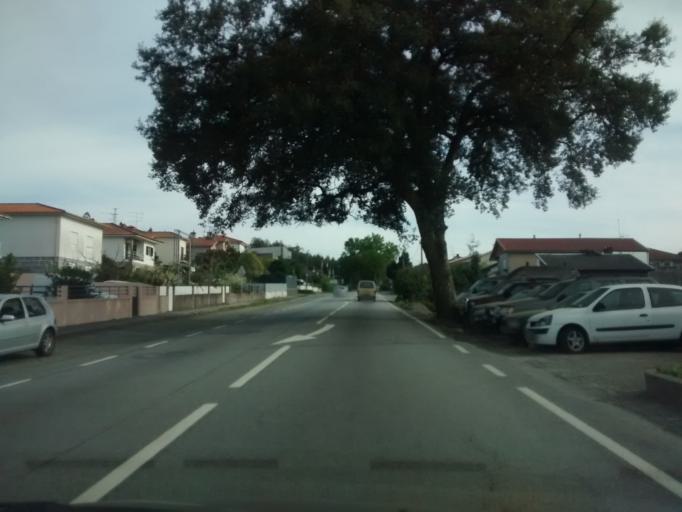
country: PT
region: Braga
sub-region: Braga
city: Braga
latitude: 41.5038
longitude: -8.4171
